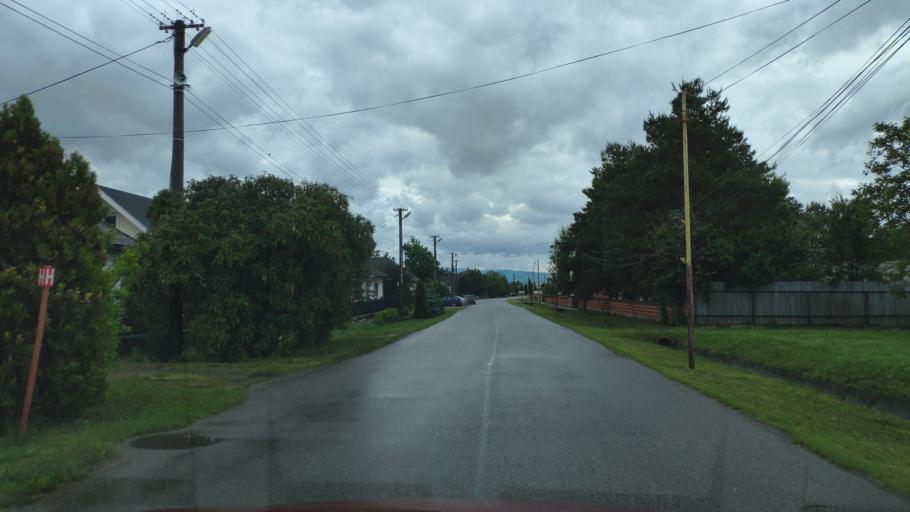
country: SK
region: Kosicky
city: Moldava nad Bodvou
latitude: 48.5372
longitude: 21.1093
